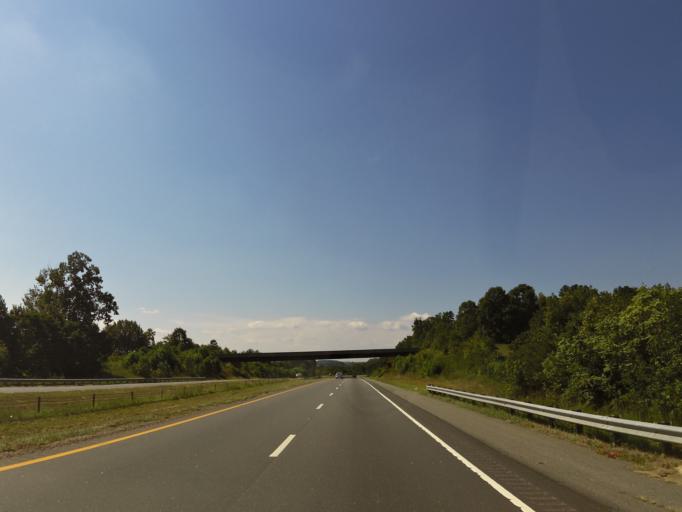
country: US
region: North Carolina
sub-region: Catawba County
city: Maiden
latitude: 35.6156
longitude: -81.2814
